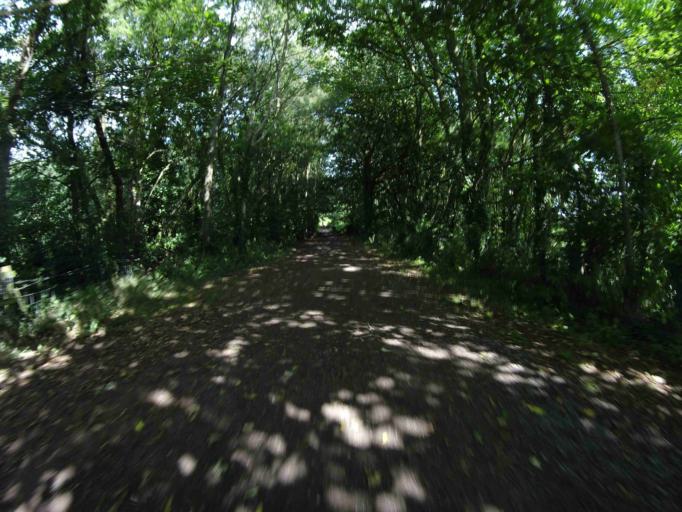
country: GB
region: England
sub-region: Devon
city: Budleigh Salterton
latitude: 50.6399
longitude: -3.3460
